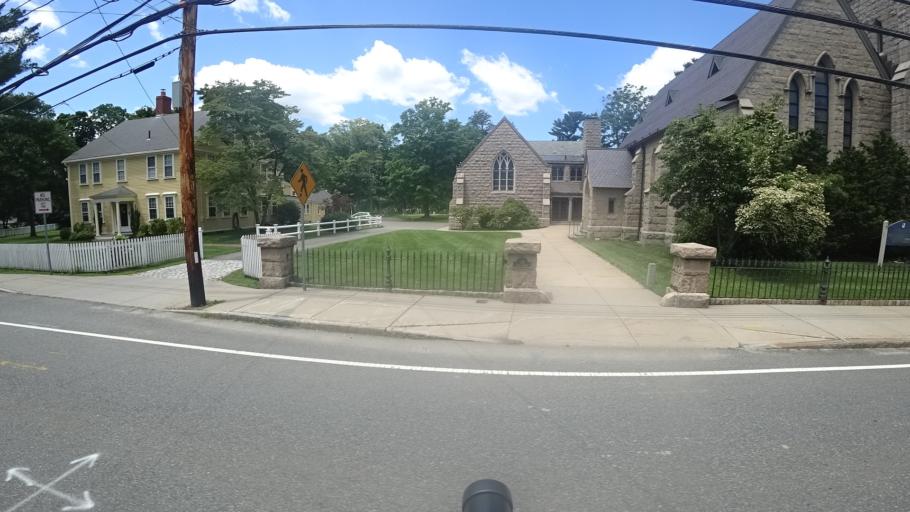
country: US
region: Massachusetts
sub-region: Norfolk County
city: Dedham
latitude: 42.2469
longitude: -71.1776
